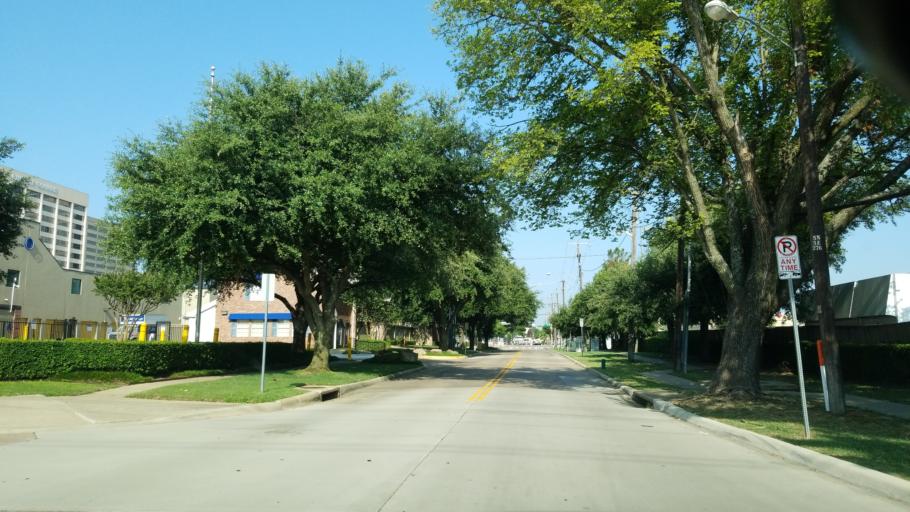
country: US
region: Texas
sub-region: Dallas County
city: Highland Park
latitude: 32.8488
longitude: -96.7679
